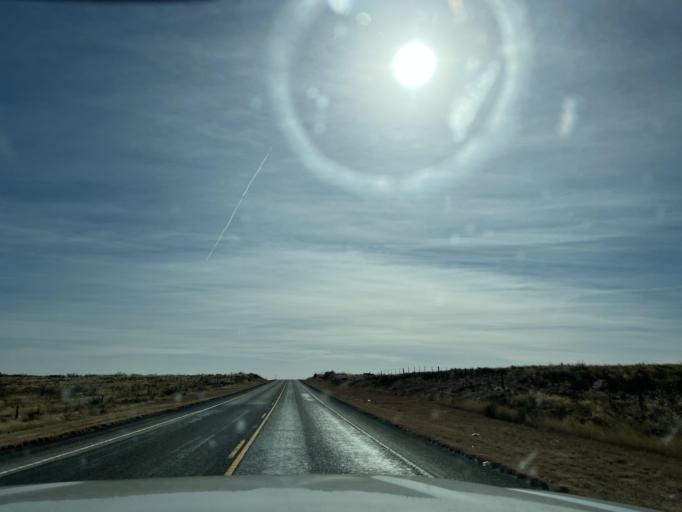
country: US
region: Texas
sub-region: Andrews County
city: Andrews
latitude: 32.4525
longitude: -102.4485
